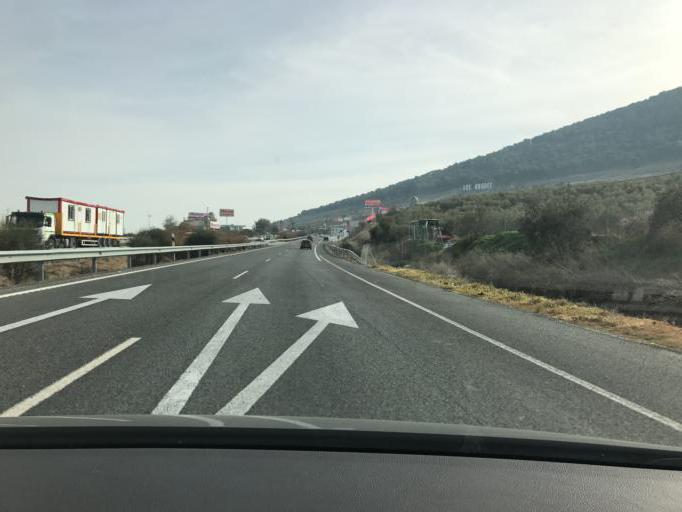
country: ES
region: Andalusia
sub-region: Provincia de Granada
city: Loja
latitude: 37.1664
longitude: -4.1744
